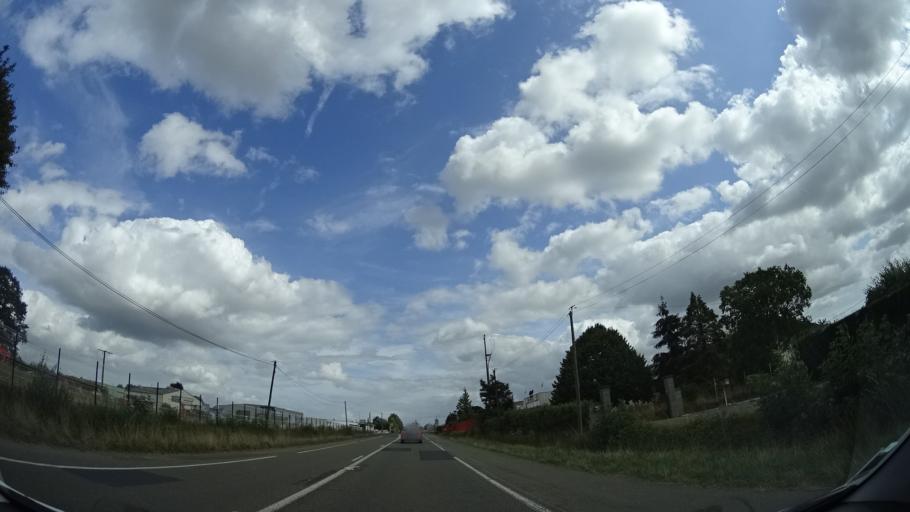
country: FR
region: Pays de la Loire
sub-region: Departement de la Mayenne
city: Soulge-sur-Ouette
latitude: 48.0610
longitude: -0.5810
